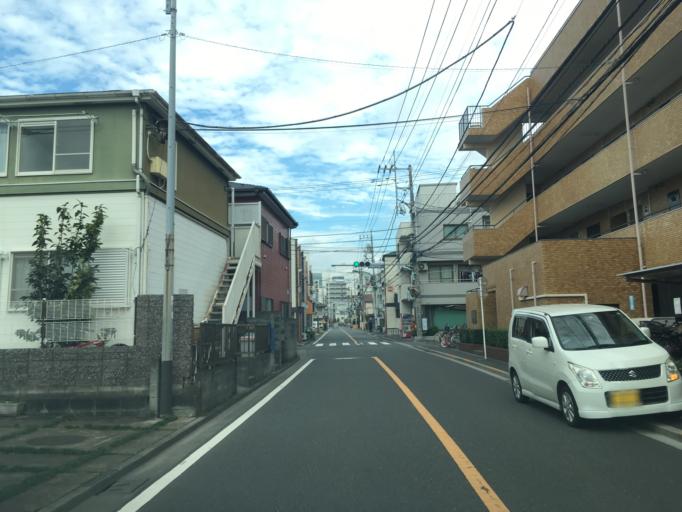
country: JP
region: Tokyo
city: Chofugaoka
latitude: 35.6471
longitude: 139.5406
